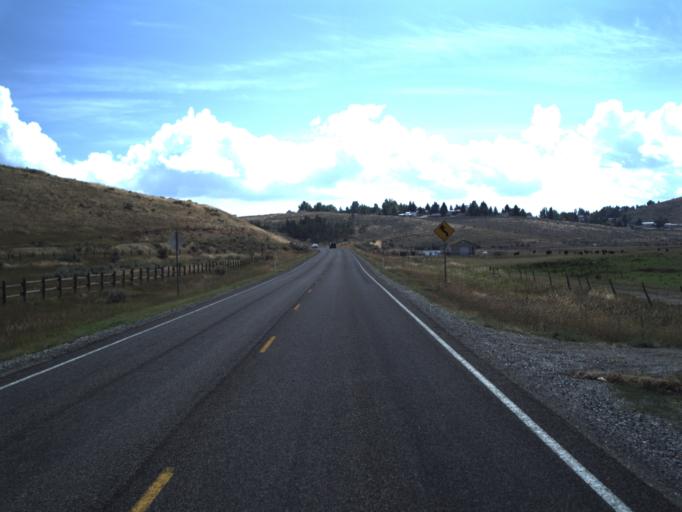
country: US
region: Utah
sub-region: Rich County
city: Randolph
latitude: 41.9040
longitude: -111.3757
